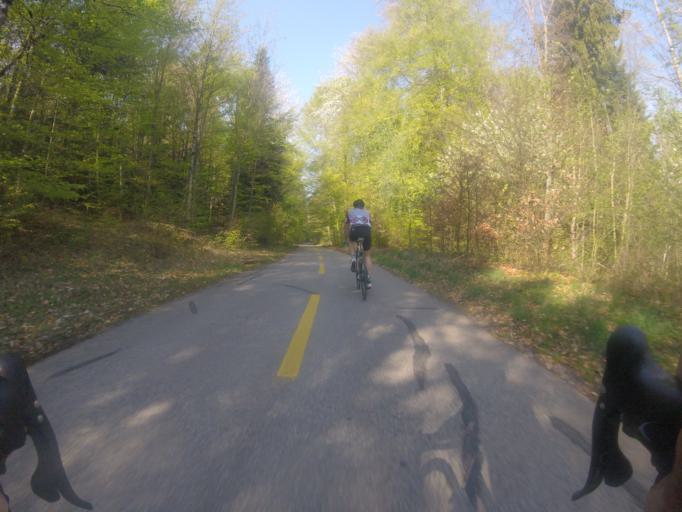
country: CH
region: Bern
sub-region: Bern-Mittelland District
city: Kirchlindach
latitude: 46.9652
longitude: 7.4028
